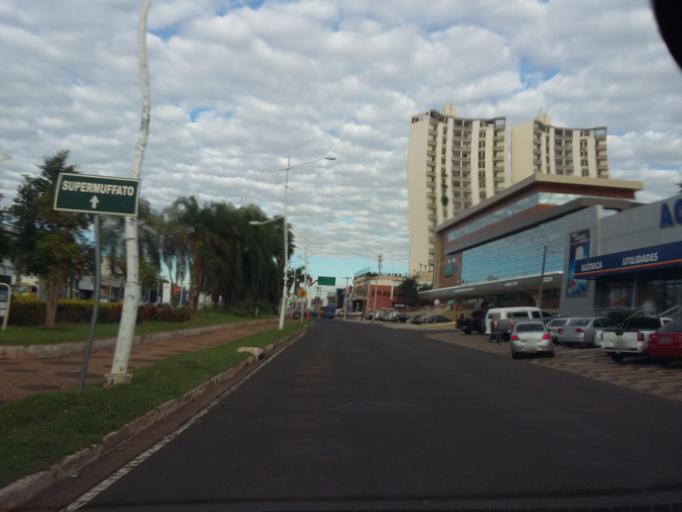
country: BR
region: Sao Paulo
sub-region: Sao Jose Do Rio Preto
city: Sao Jose do Rio Preto
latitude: -20.8188
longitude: -49.3967
